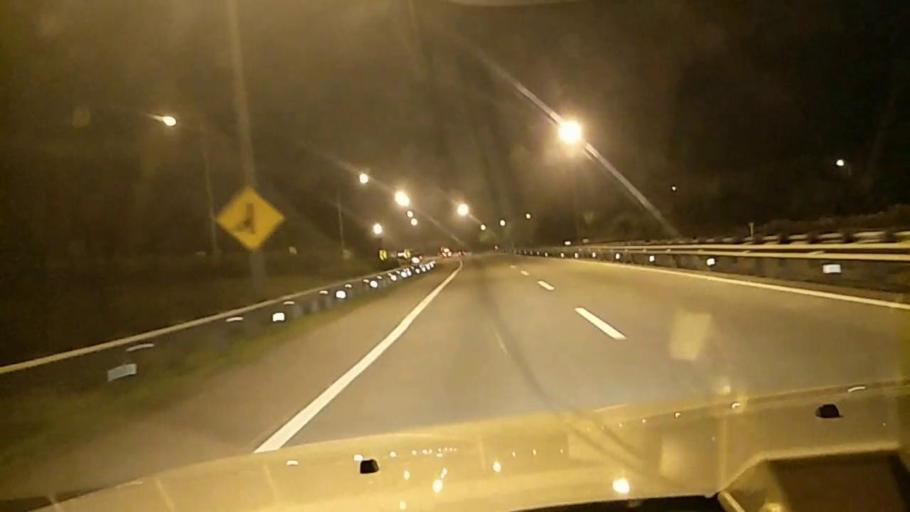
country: MY
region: Perak
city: Parit Buntar
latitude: 5.1089
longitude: 100.5580
